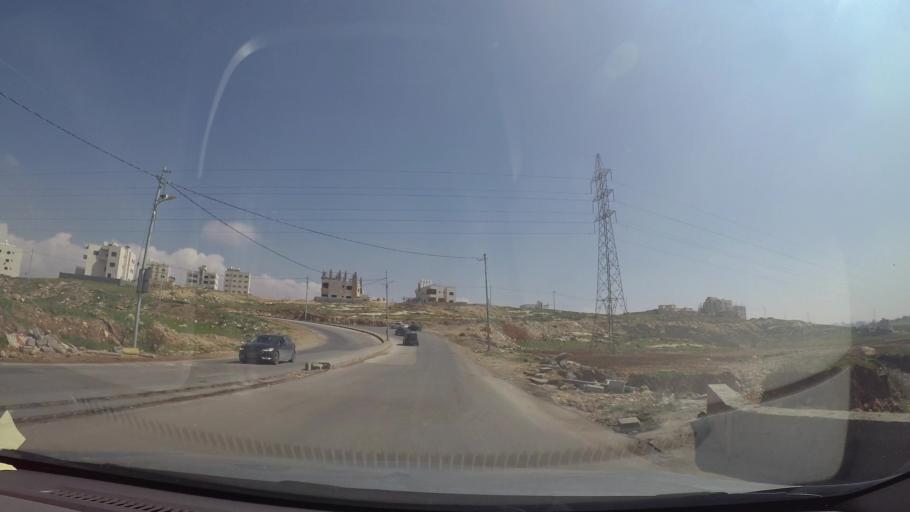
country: JO
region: Amman
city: Al Bunayyat ash Shamaliyah
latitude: 31.8879
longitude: 35.9011
